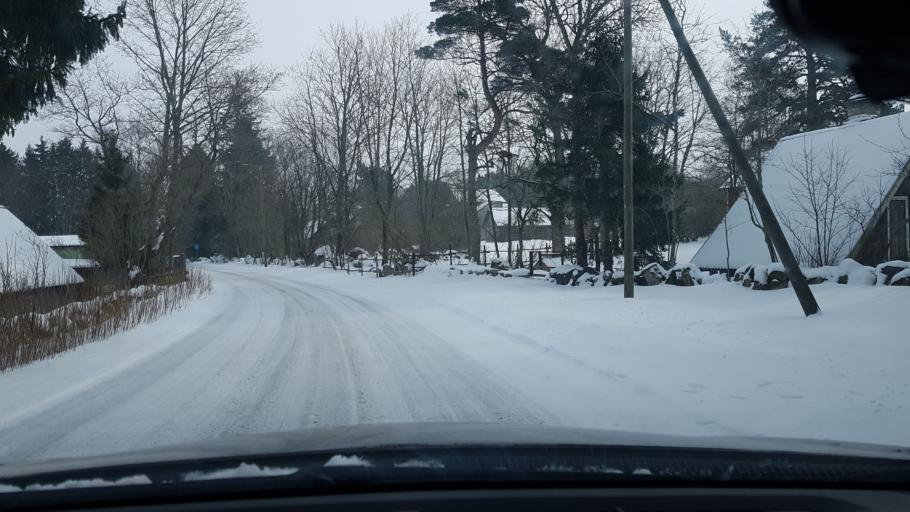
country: EE
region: Harju
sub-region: Kuusalu vald
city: Kuusalu
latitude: 59.4916
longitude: 25.3786
